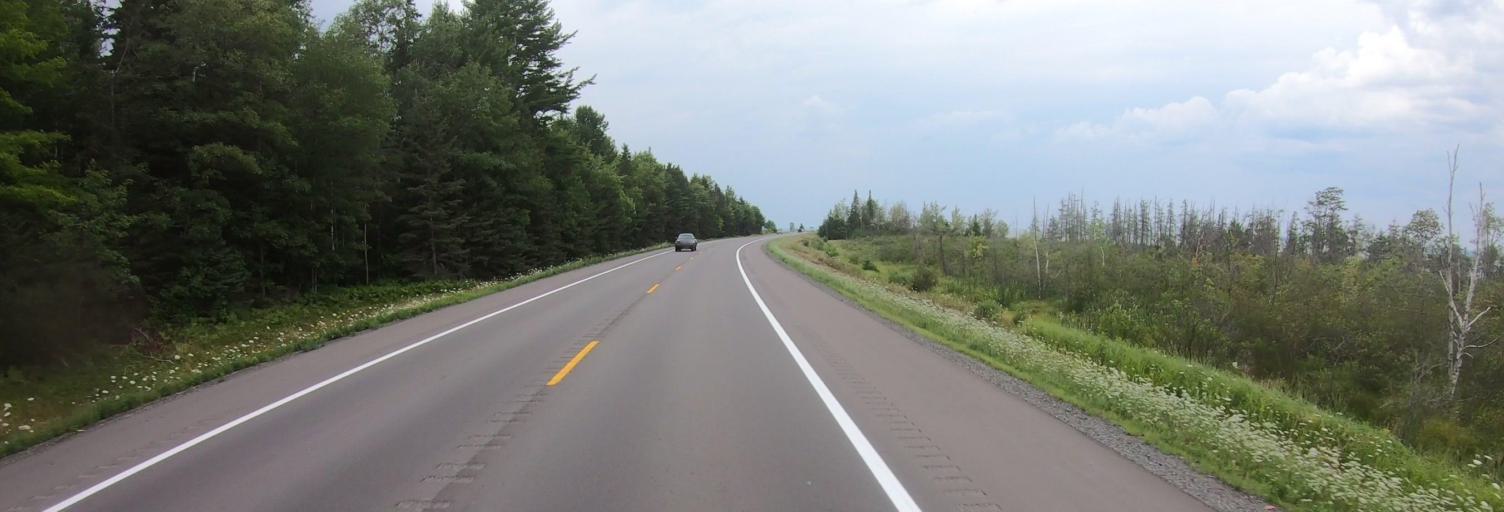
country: US
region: Michigan
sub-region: Baraga County
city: Baraga
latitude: 46.8046
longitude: -88.4756
